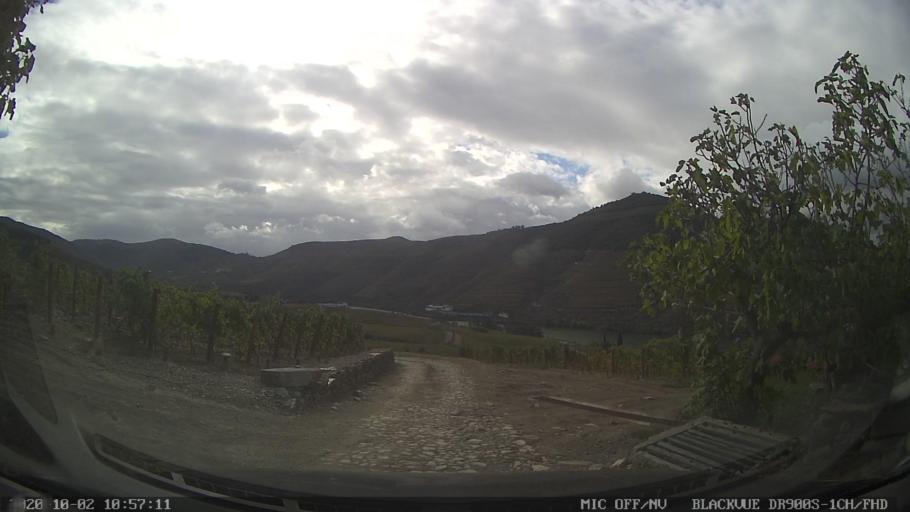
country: PT
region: Vila Real
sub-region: Sabrosa
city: Vilela
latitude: 41.1918
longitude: -7.5371
